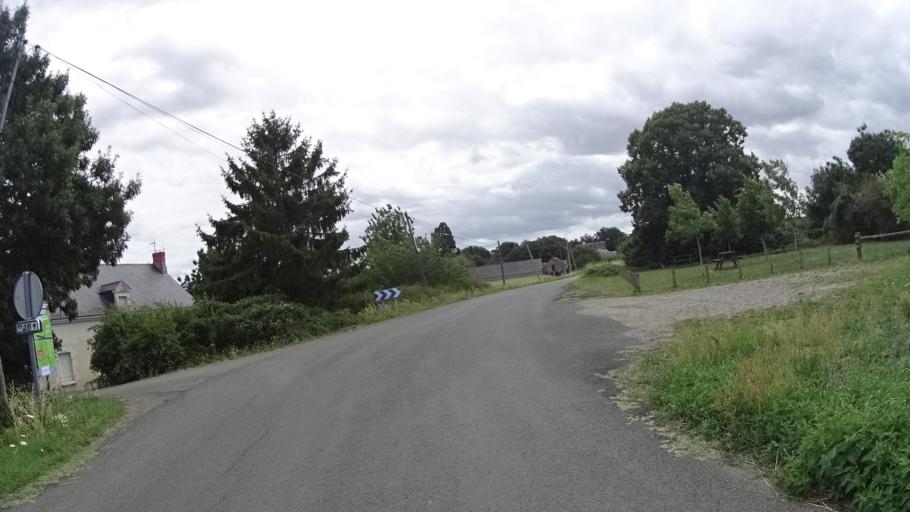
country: FR
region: Pays de la Loire
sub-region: Departement de Maine-et-Loire
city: Les Ponts-de-Ce
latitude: 47.4241
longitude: -0.4980
